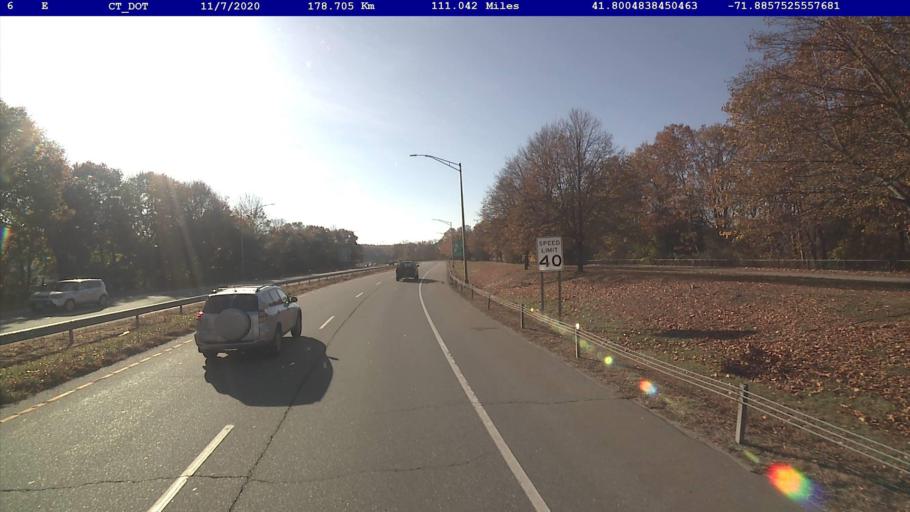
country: US
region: Connecticut
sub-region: Windham County
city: Danielson
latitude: 41.8005
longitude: -71.8859
